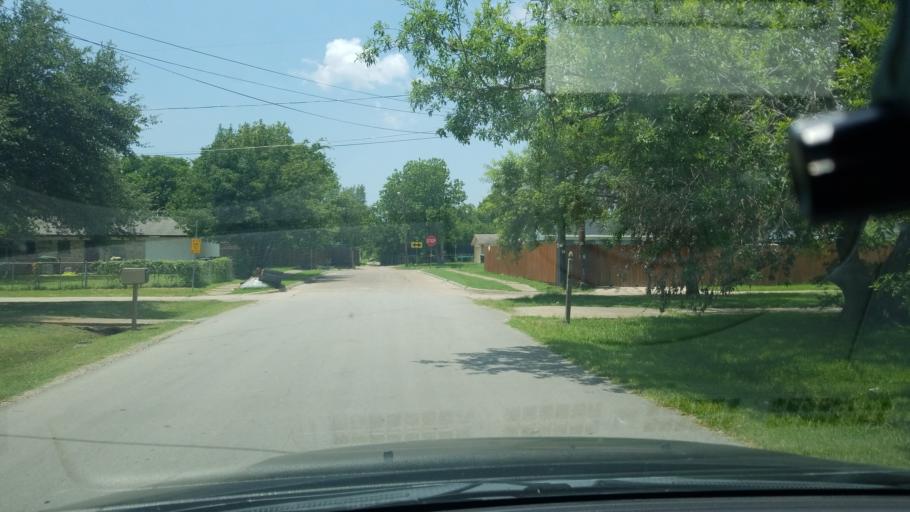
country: US
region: Texas
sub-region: Dallas County
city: Balch Springs
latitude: 32.7136
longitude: -96.6493
